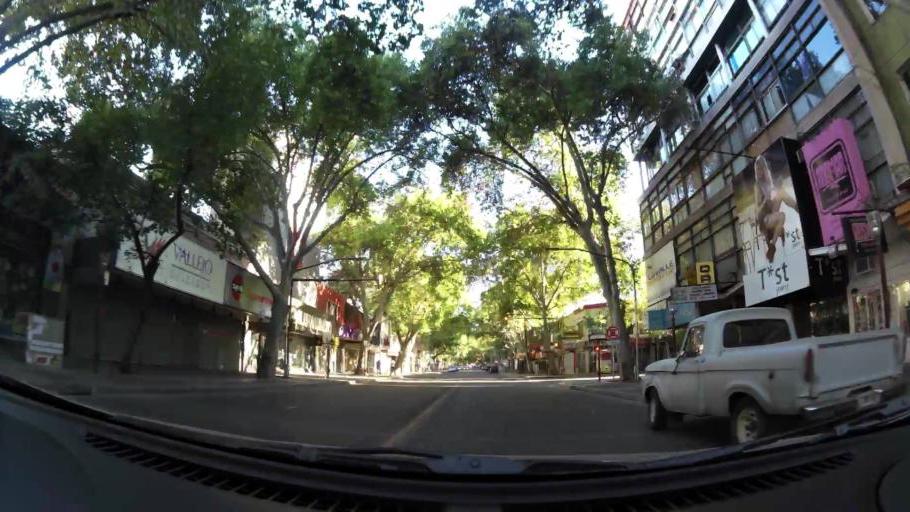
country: AR
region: Mendoza
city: Mendoza
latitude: -32.8850
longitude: -68.8380
